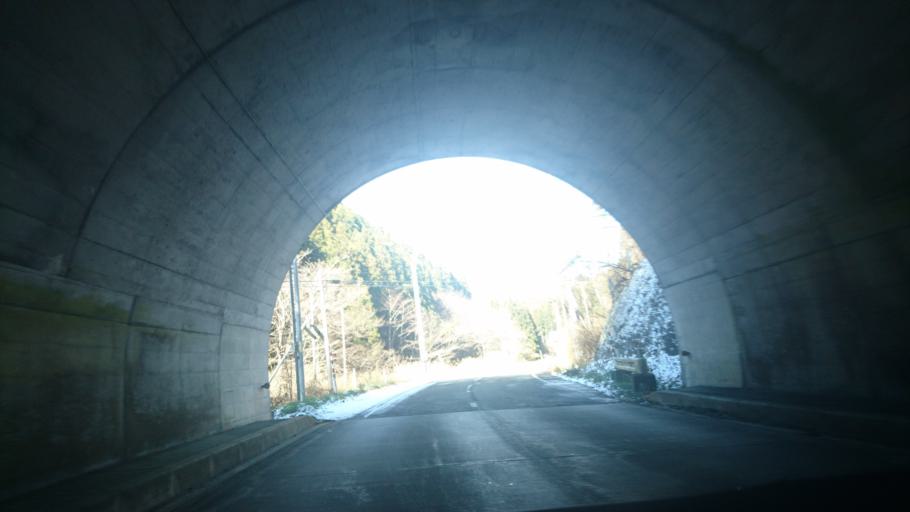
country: JP
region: Iwate
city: Mizusawa
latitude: 39.0881
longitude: 141.3858
